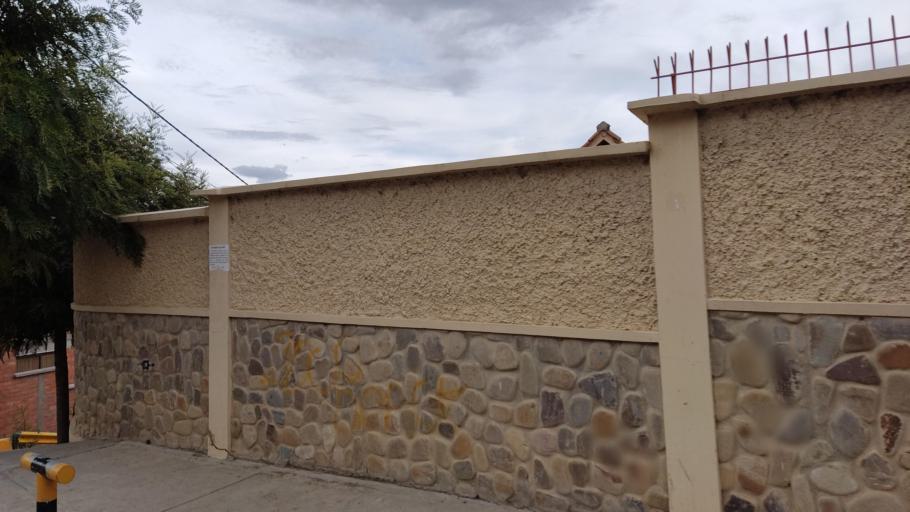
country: BO
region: La Paz
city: La Paz
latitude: -16.5641
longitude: -68.0999
